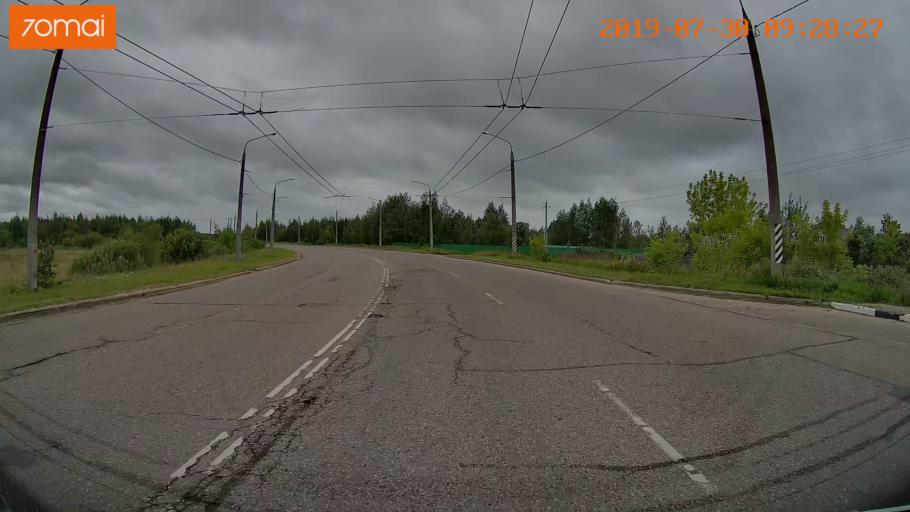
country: RU
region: Ivanovo
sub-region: Gorod Ivanovo
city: Ivanovo
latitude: 56.9530
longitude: 40.9524
